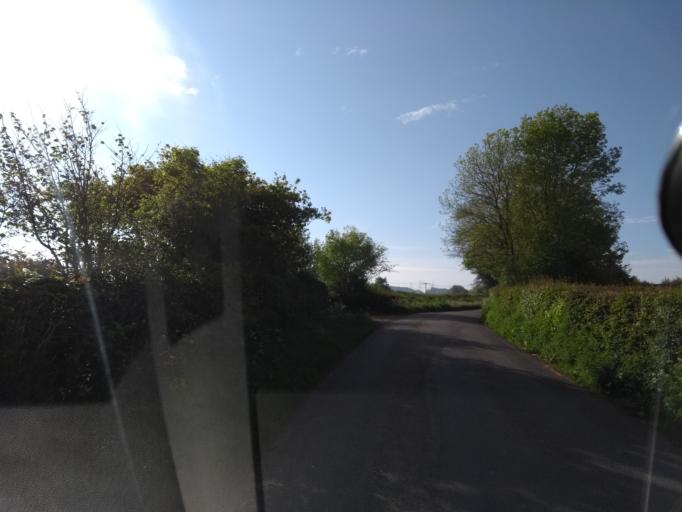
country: GB
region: England
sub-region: Dorset
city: Lyme Regis
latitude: 50.7966
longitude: -2.9286
